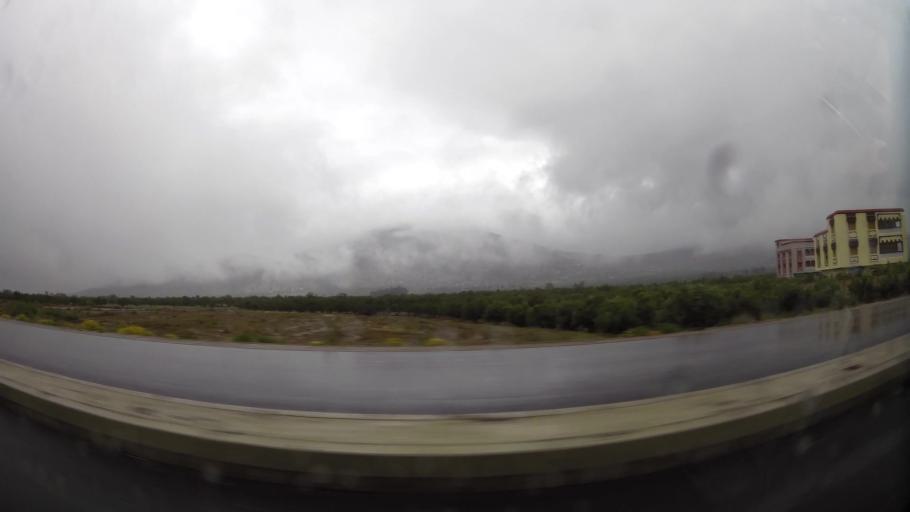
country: MA
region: Oriental
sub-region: Nador
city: Midar
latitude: 34.8372
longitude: -3.7205
